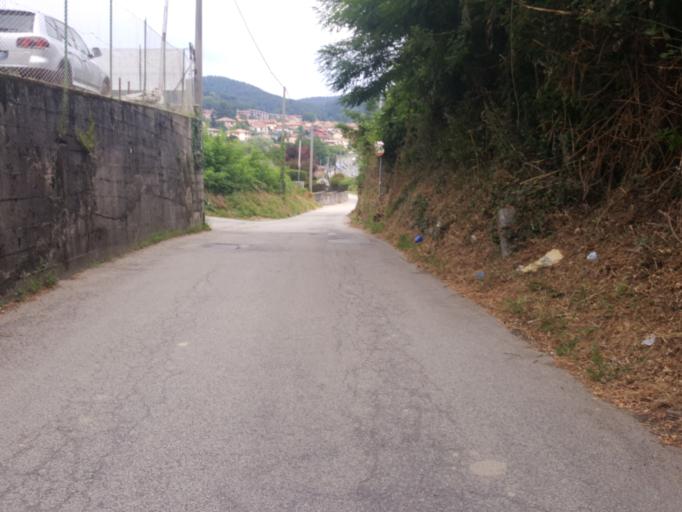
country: IT
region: Lombardy
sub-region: Provincia di Varese
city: Mercallo
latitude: 45.7437
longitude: 8.6737
